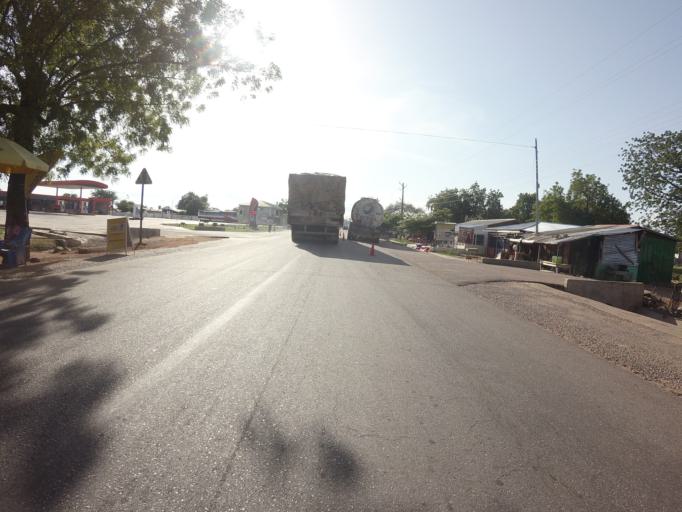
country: GH
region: Upper East
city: Navrongo
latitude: 10.8940
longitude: -1.0825
